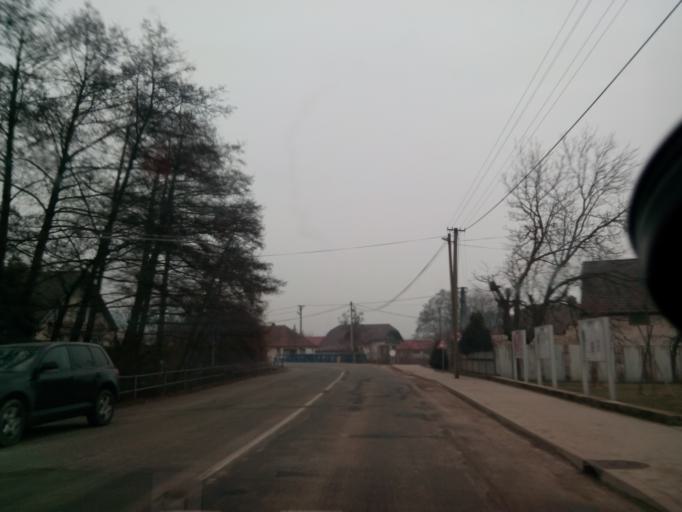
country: SK
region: Kosicky
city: Kosice
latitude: 48.6767
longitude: 21.1657
